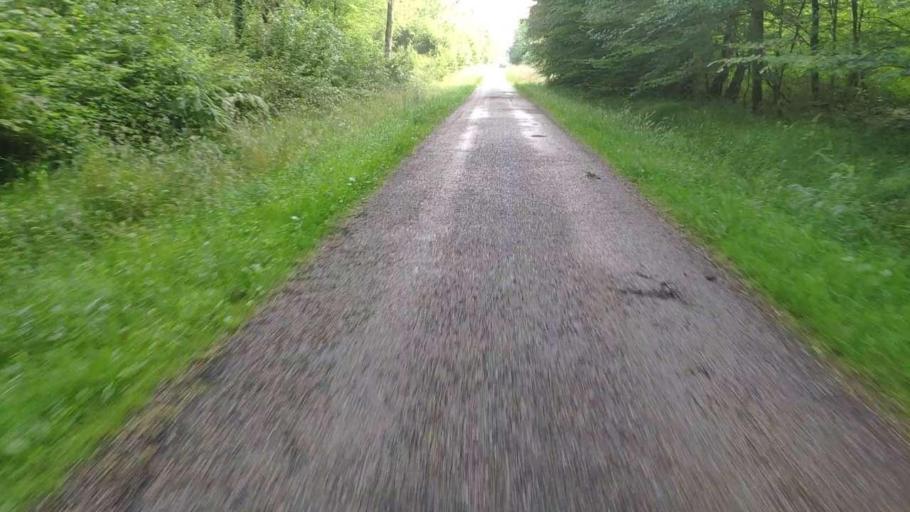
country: FR
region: Franche-Comte
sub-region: Departement du Jura
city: Mont-sous-Vaudrey
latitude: 46.8819
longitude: 5.5232
